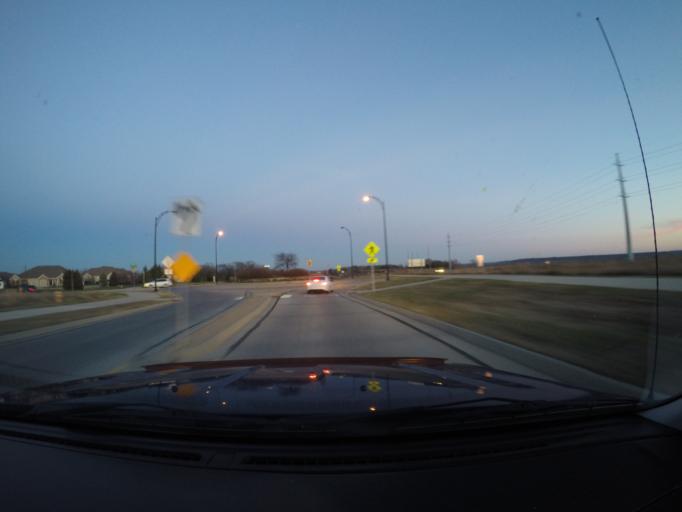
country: US
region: Kansas
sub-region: Douglas County
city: Lawrence
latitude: 38.9430
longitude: -95.3300
